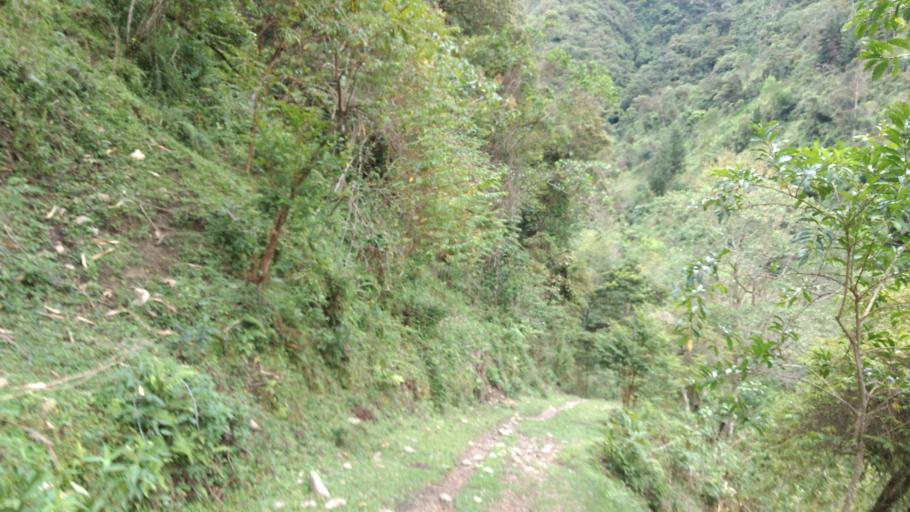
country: CO
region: Tolima
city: Cajamarca
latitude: 4.5480
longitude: -75.3329
